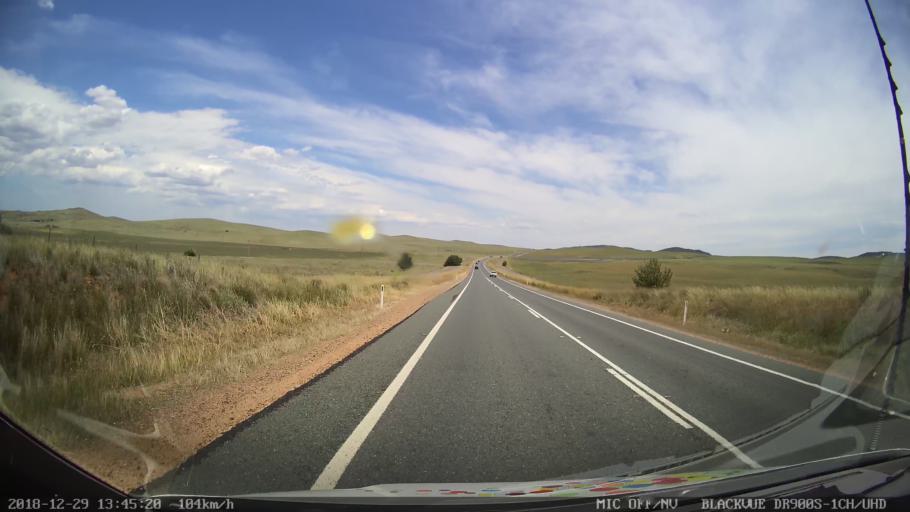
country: AU
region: New South Wales
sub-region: Cooma-Monaro
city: Cooma
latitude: -36.0948
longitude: 149.1453
